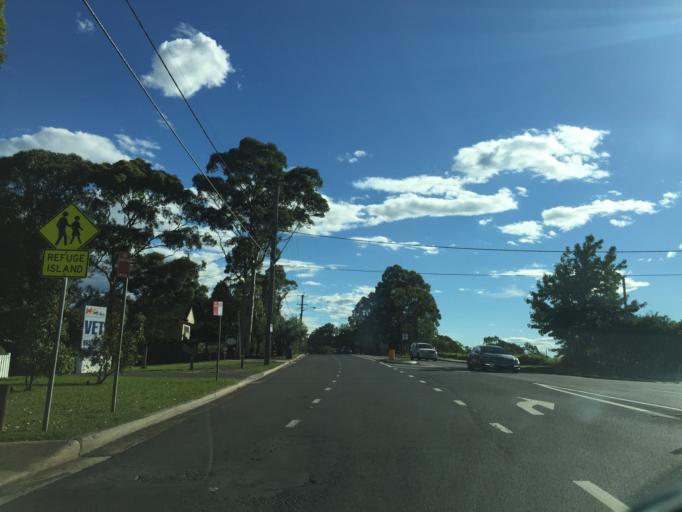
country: AU
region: New South Wales
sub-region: The Hills Shire
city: Glenhaven
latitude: -33.6941
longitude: 151.0188
